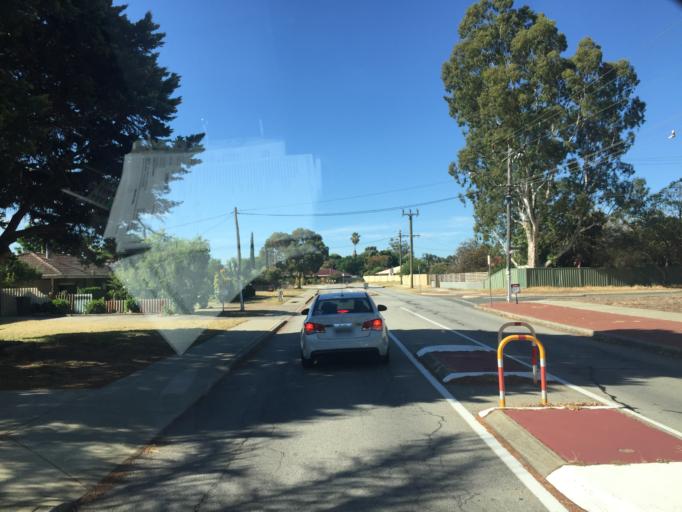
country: AU
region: Western Australia
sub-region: Gosnells
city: Maddington
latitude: -32.0525
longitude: 115.9999
